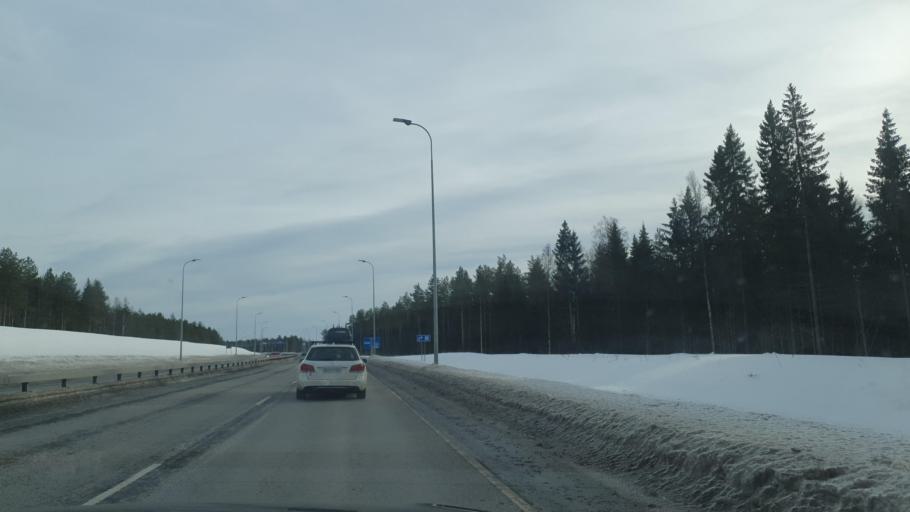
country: FI
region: Northern Ostrobothnia
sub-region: Oulu
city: Kempele
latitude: 64.9839
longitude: 25.5510
